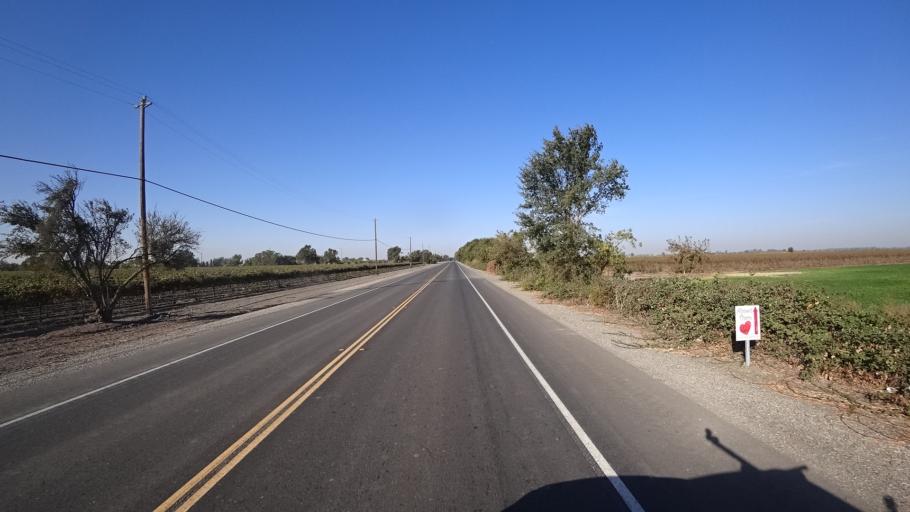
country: US
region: California
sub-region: Sacramento County
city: Parkway
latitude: 38.4144
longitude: -121.5524
